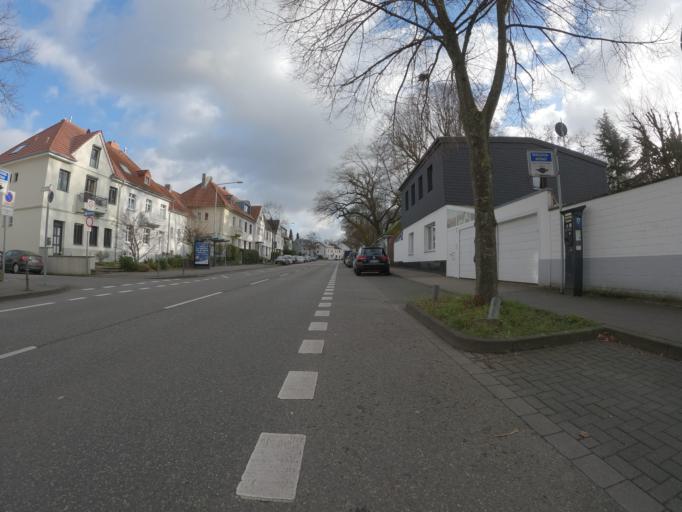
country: DE
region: North Rhine-Westphalia
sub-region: Regierungsbezirk Koln
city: Aachen
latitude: 50.7873
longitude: 6.0956
